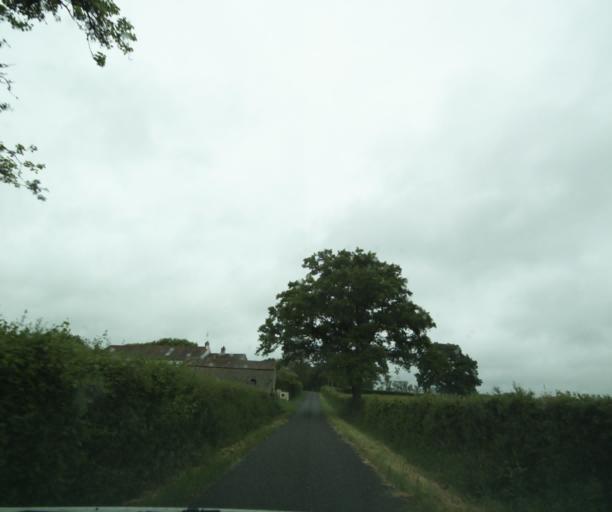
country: FR
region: Bourgogne
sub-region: Departement de Saone-et-Loire
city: Palinges
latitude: 46.5500
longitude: 4.1972
